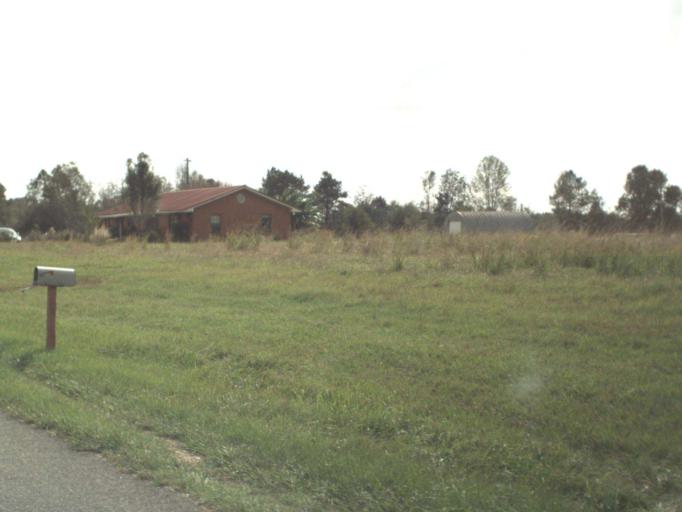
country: US
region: Alabama
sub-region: Escambia County
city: East Brewton
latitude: 30.9412
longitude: -87.0287
